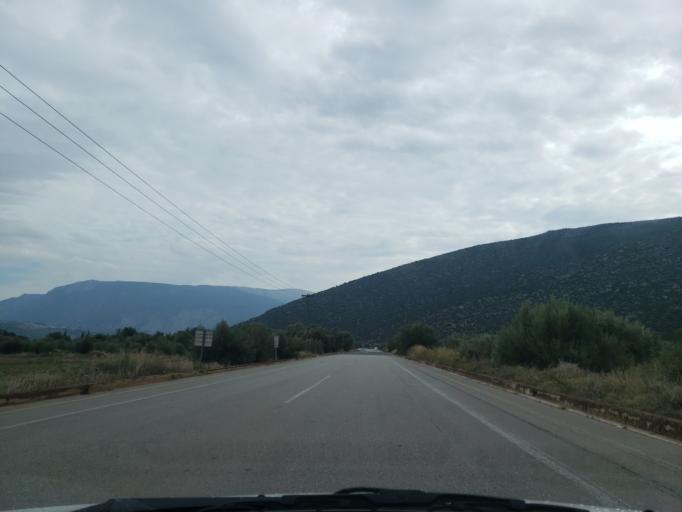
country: GR
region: Central Greece
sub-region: Nomos Fokidos
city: Itea
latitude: 38.4875
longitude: 22.4194
